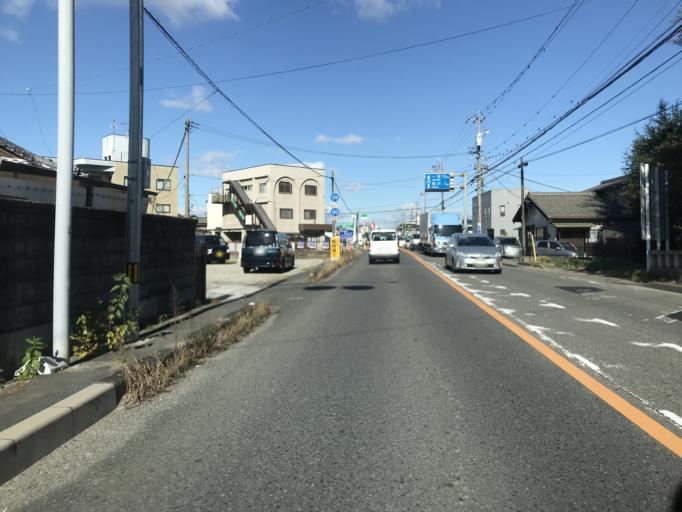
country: JP
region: Aichi
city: Inazawa
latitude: 35.2209
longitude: 136.8425
